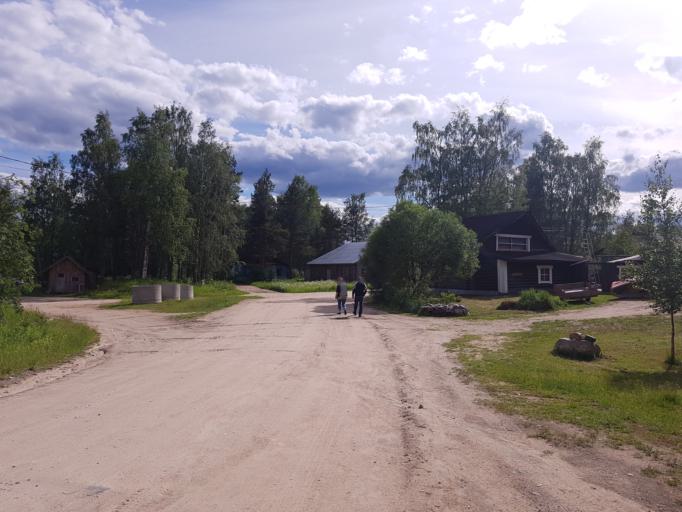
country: RU
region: Republic of Karelia
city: Kostomuksha
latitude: 64.9534
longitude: 30.5580
